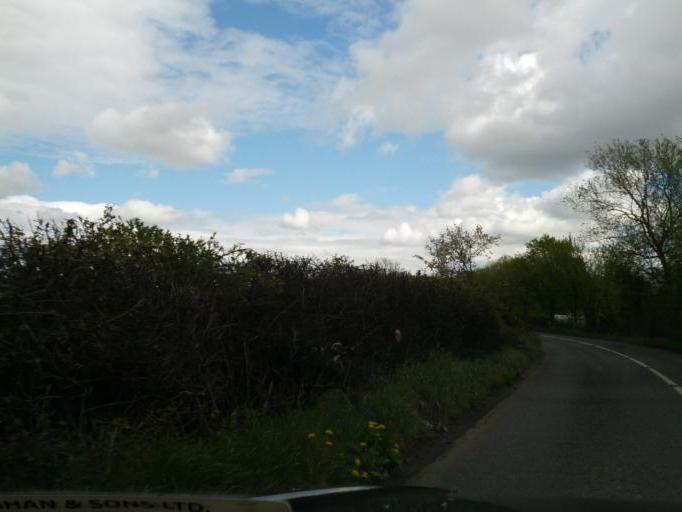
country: IE
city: Confey
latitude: 53.3740
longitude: -6.4745
